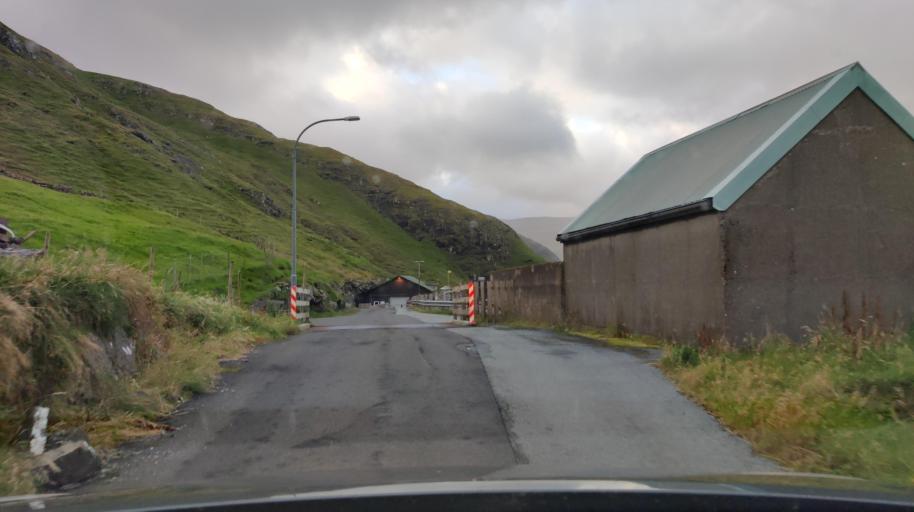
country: FO
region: Streymoy
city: Vestmanna
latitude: 62.1494
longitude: -7.1603
